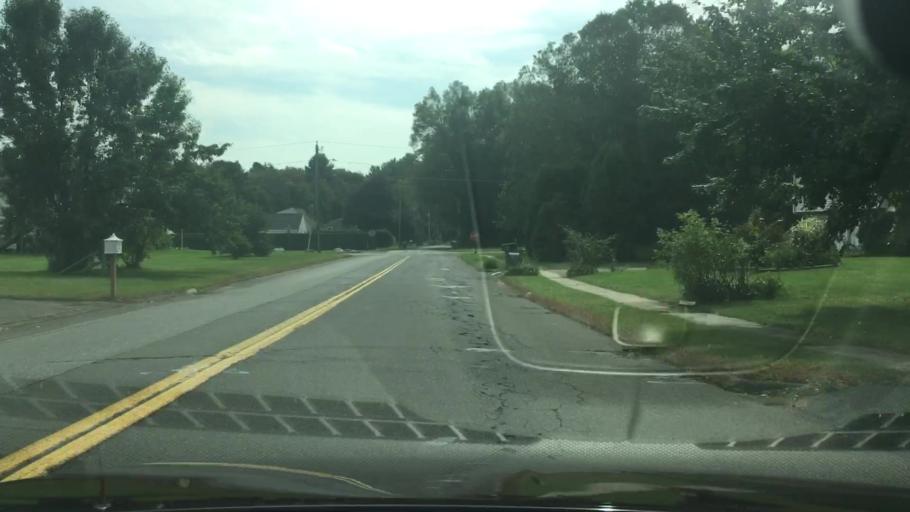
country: US
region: Connecticut
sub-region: Hartford County
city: Hazardville
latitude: 42.0067
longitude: -72.5105
